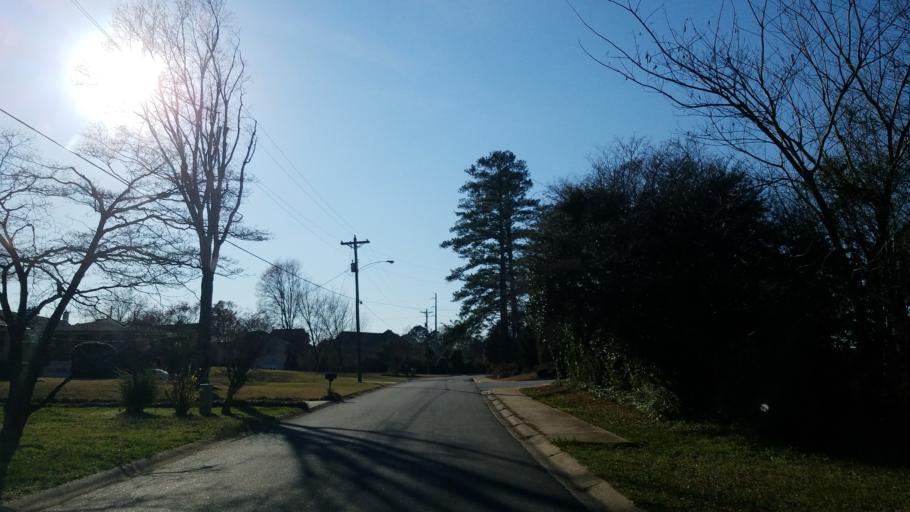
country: US
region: Georgia
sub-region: Cobb County
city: Marietta
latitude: 33.9998
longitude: -84.5011
